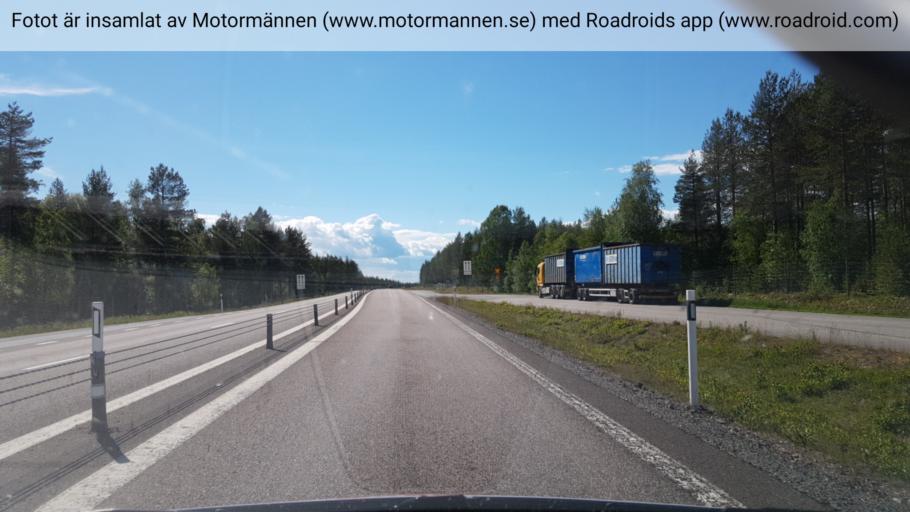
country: SE
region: Norrbotten
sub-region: Kalix Kommun
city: Toere
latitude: 65.9134
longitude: 22.7032
